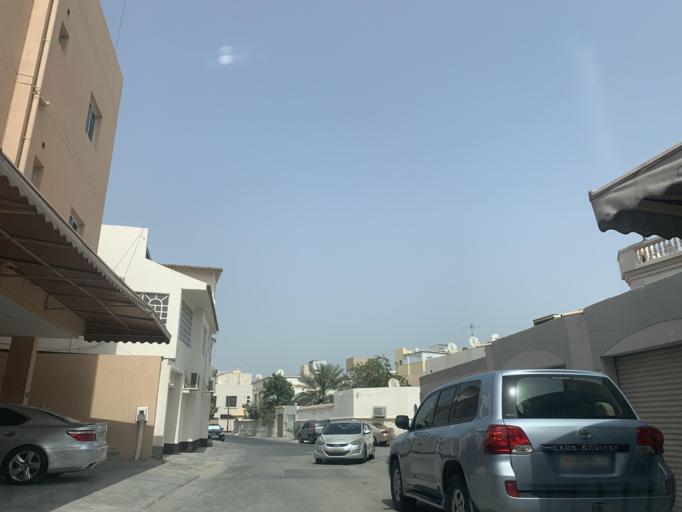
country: BH
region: Northern
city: Madinat `Isa
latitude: 26.1749
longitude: 50.5585
